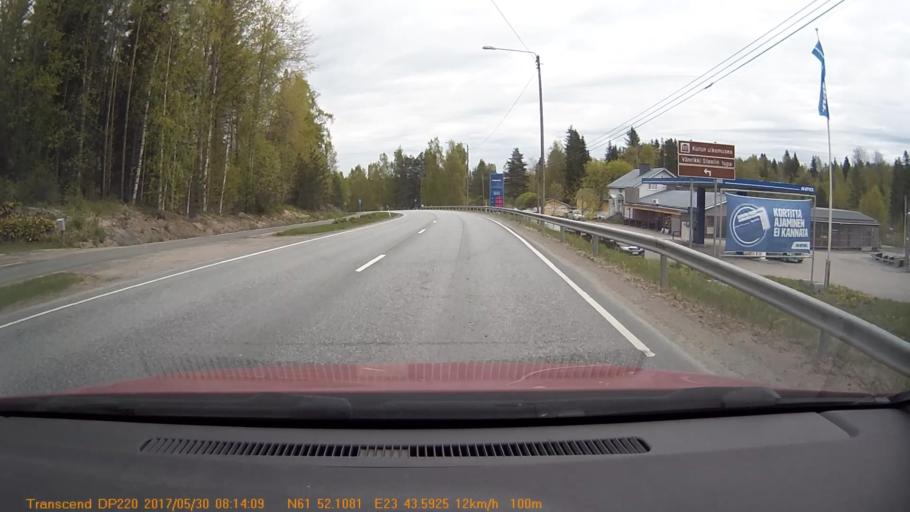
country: FI
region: Pirkanmaa
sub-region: Tampere
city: Kuru
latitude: 61.8686
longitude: 23.7265
